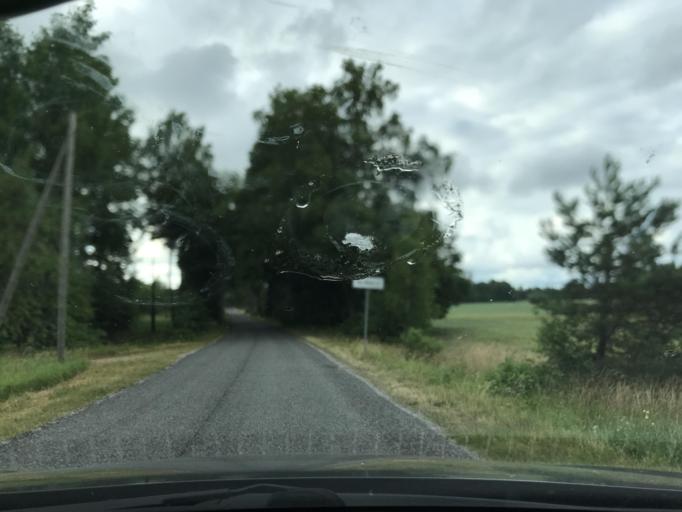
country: LV
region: Alsunga
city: Alsunga
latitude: 56.9771
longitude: 21.6393
